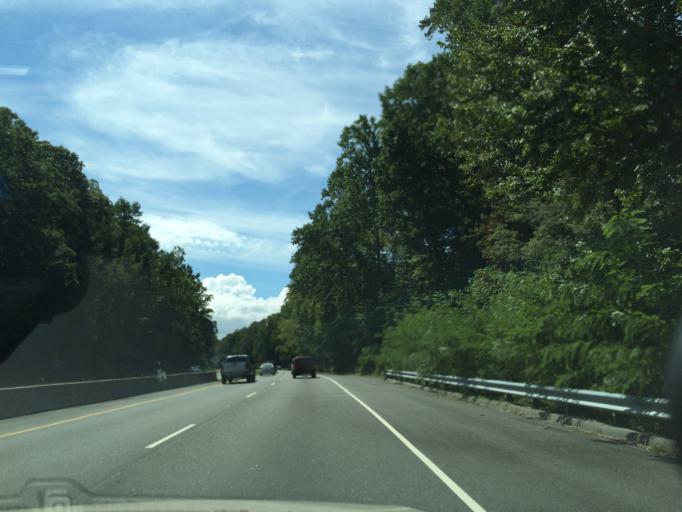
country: US
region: Virginia
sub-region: York County
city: Yorktown
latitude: 37.2322
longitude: -76.5139
